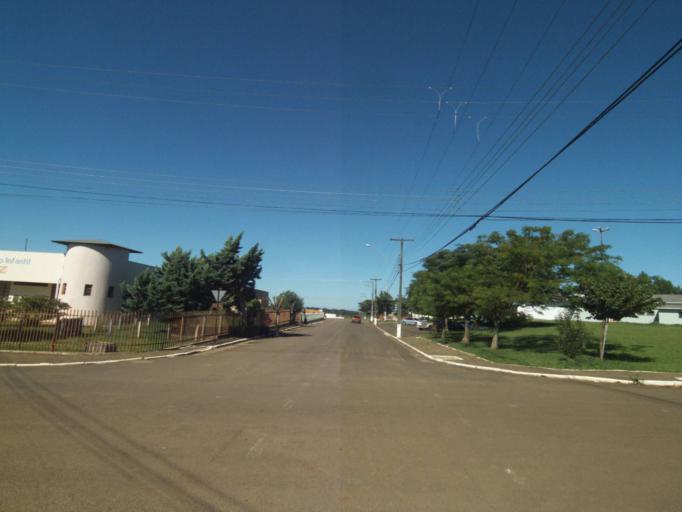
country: BR
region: Parana
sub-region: Pinhao
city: Pinhao
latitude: -25.8348
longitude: -52.0295
